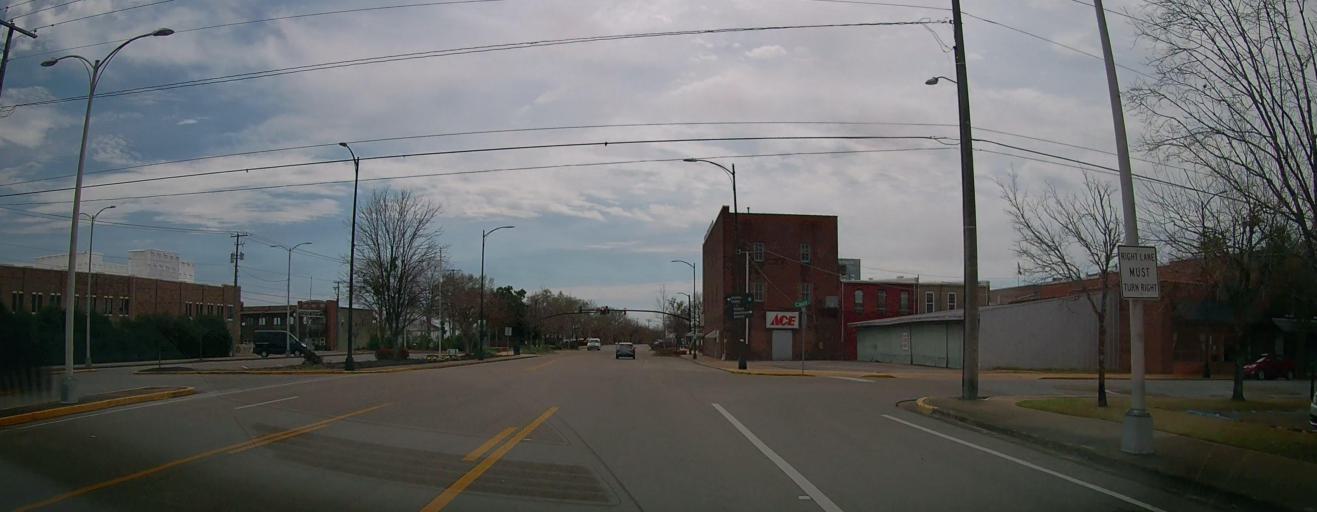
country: US
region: Mississippi
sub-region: Lee County
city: Tupelo
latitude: 34.2585
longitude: -88.7035
